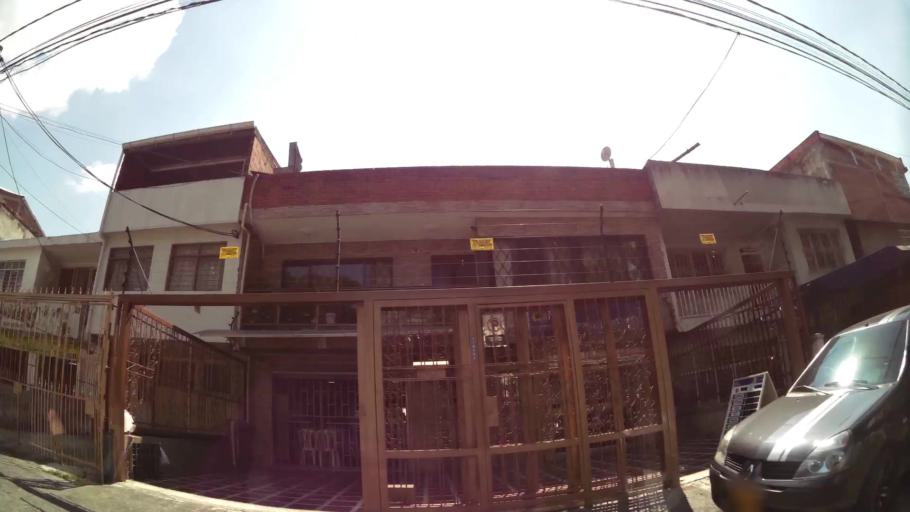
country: CO
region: Valle del Cauca
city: Cali
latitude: 3.4251
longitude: -76.5275
